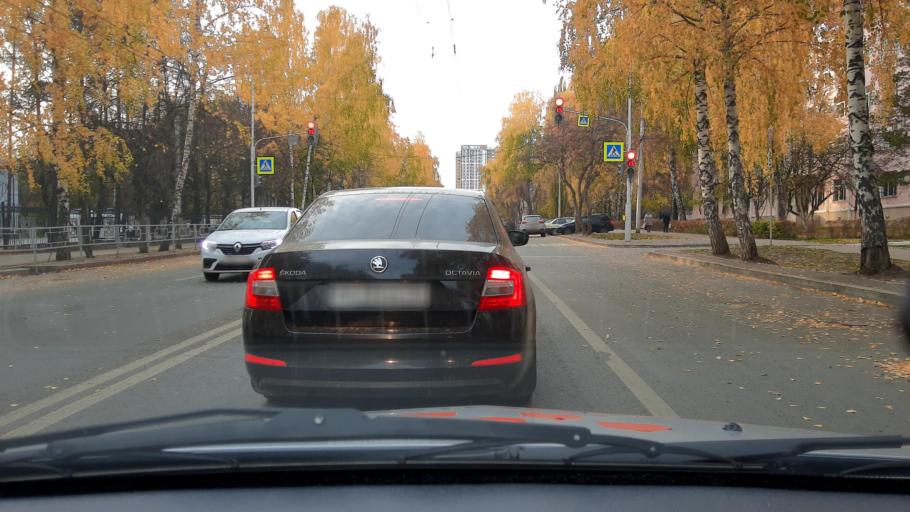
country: RU
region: Bashkortostan
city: Ufa
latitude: 54.7617
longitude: 56.0081
